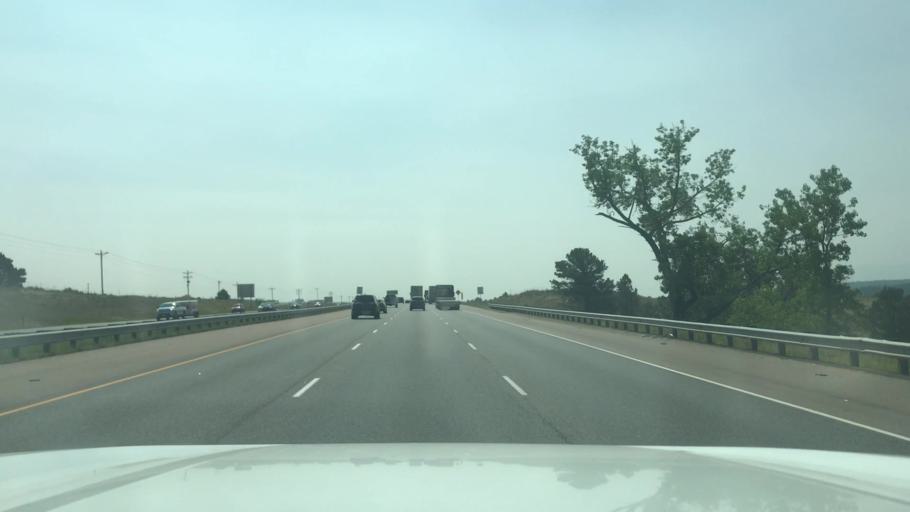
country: US
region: Colorado
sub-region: El Paso County
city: Gleneagle
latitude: 39.0483
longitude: -104.8473
